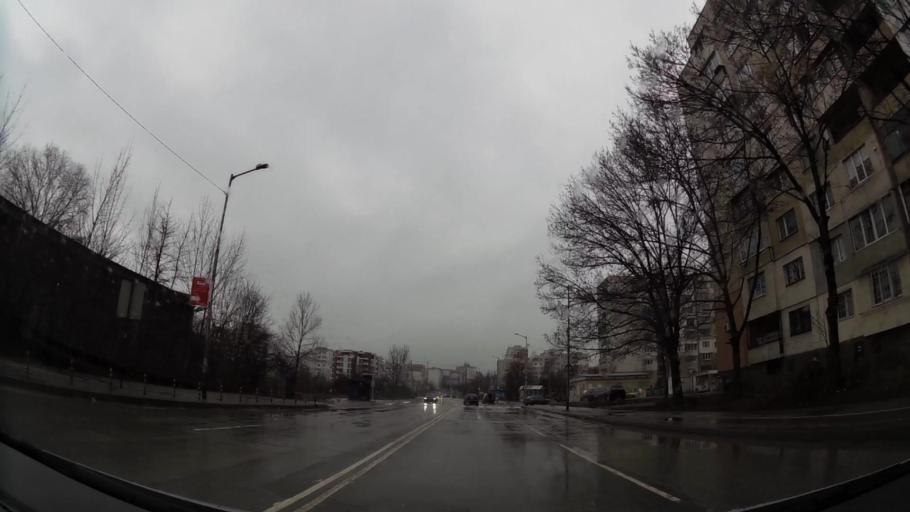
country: BG
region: Sofia-Capital
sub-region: Stolichna Obshtina
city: Sofia
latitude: 42.6327
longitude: 23.3803
